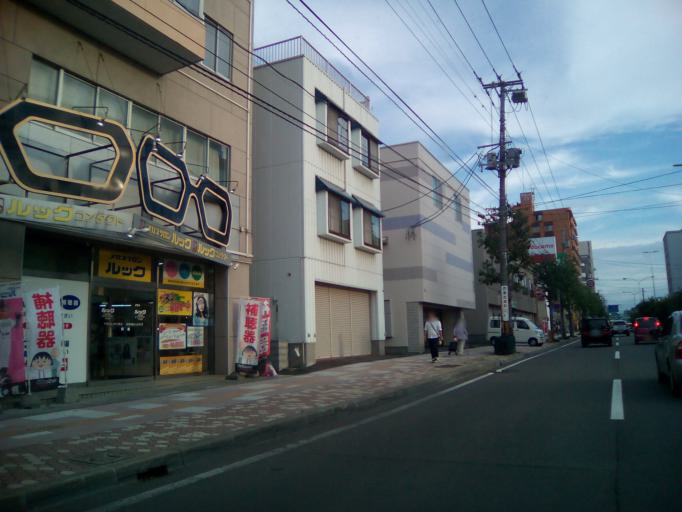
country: JP
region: Hokkaido
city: Sapporo
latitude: 43.0289
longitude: 141.3683
